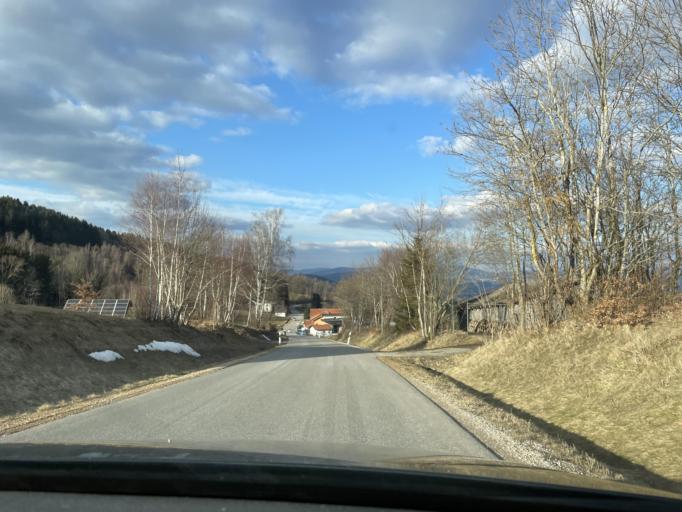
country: DE
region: Bavaria
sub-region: Lower Bavaria
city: Kollnburg
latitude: 49.0261
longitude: 12.8618
